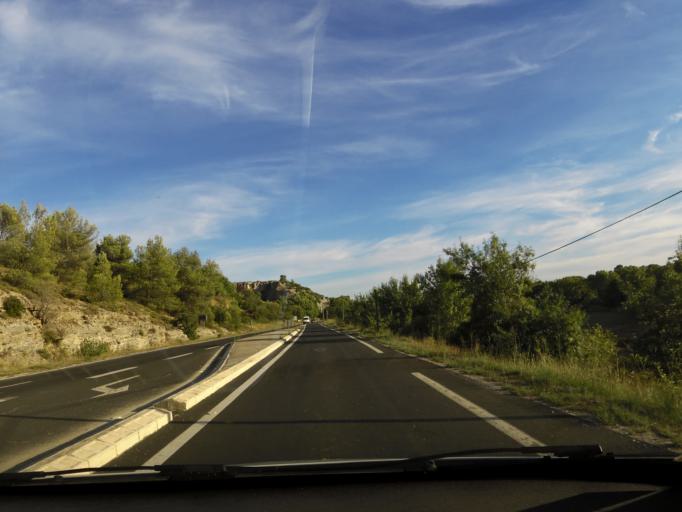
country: FR
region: Languedoc-Roussillon
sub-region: Departement de l'Herault
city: Prades-le-Lez
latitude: 43.7123
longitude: 3.8669
